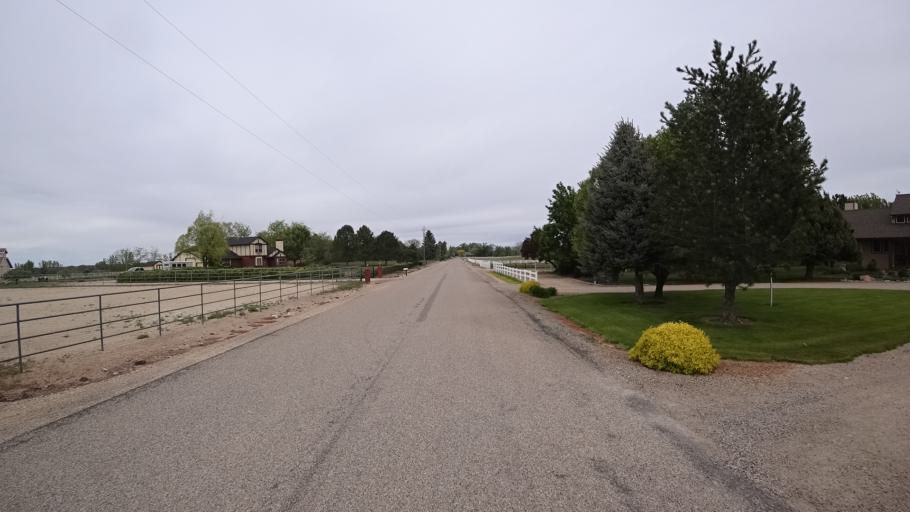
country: US
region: Idaho
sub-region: Ada County
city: Kuna
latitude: 43.4992
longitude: -116.3395
